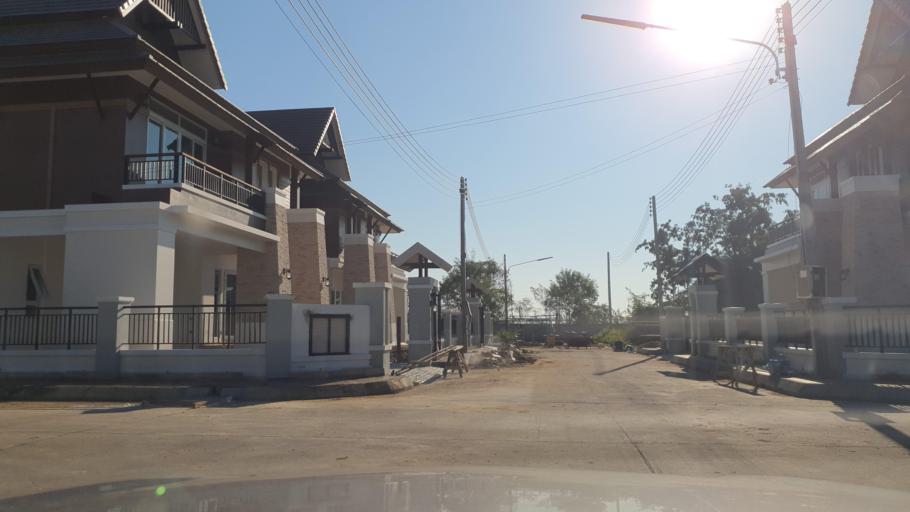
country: TH
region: Chiang Mai
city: Hang Dong
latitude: 18.6965
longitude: 98.9601
